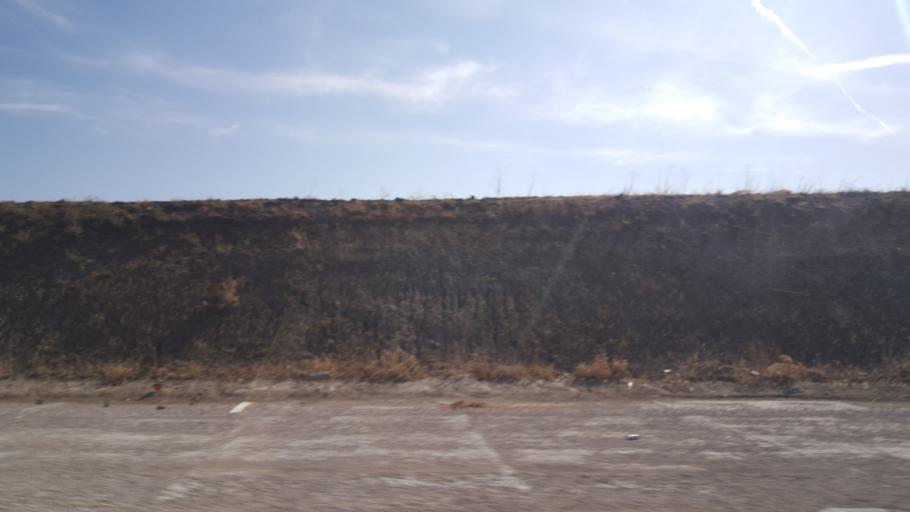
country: TR
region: Ankara
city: Yenice
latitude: 39.3808
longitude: 32.7796
